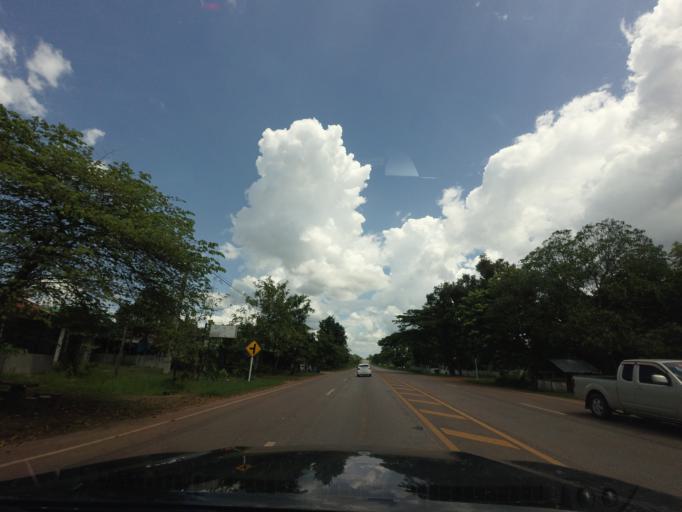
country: TH
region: Changwat Udon Thani
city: Ban Dung
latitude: 17.6860
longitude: 103.2031
